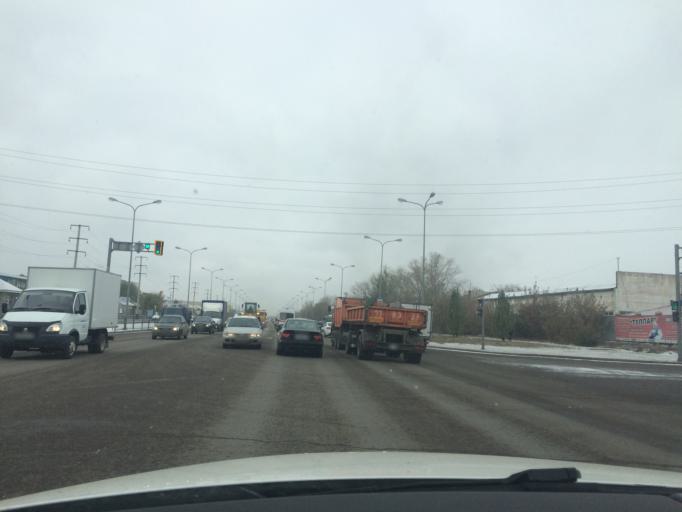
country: KZ
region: Astana Qalasy
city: Astana
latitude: 51.1788
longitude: 71.4691
